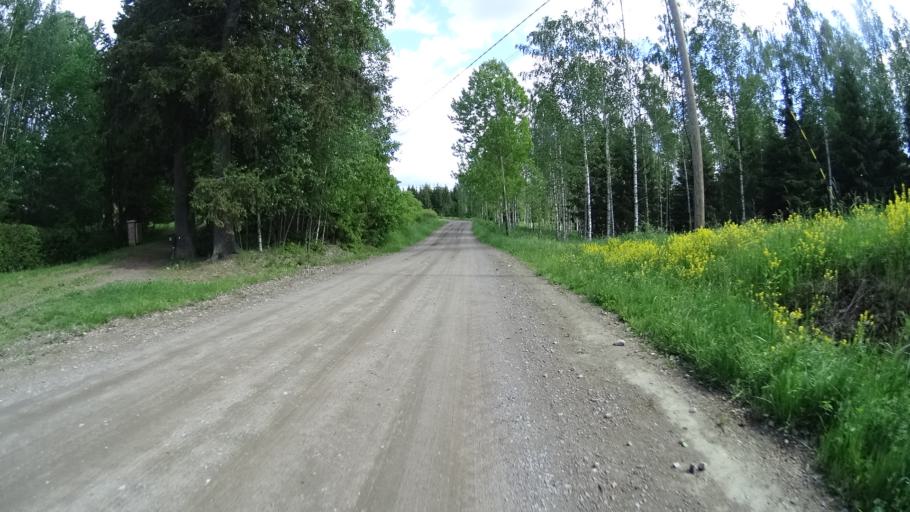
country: FI
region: Uusimaa
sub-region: Raaseporin
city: Pohja
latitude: 60.1212
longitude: 23.5911
